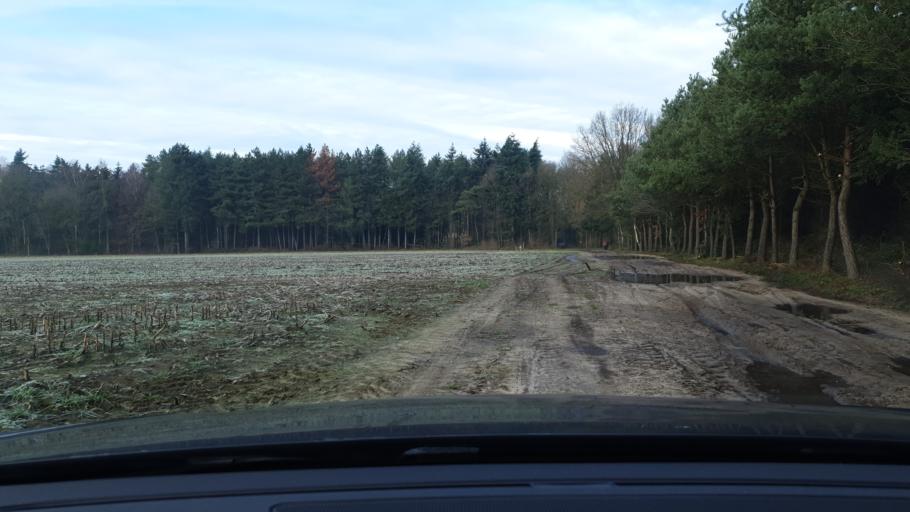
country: NL
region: North Brabant
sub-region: Gemeente Veldhoven
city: Oerle
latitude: 51.4295
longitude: 5.3502
